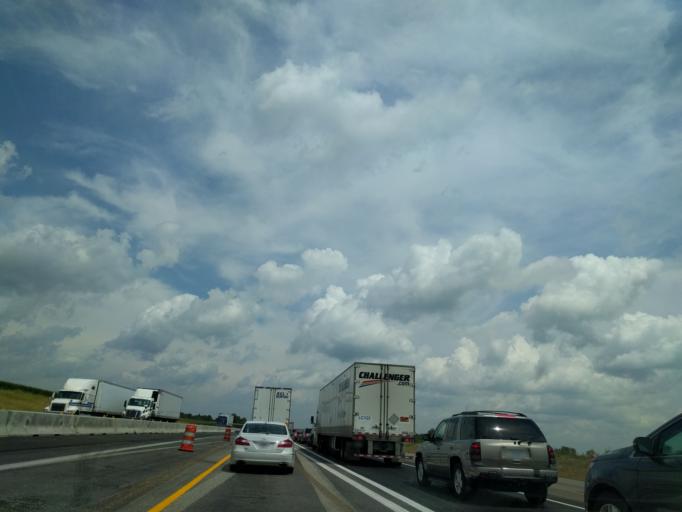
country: US
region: Kentucky
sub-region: Larue County
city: Hodgenville
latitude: 37.5491
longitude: -85.8788
